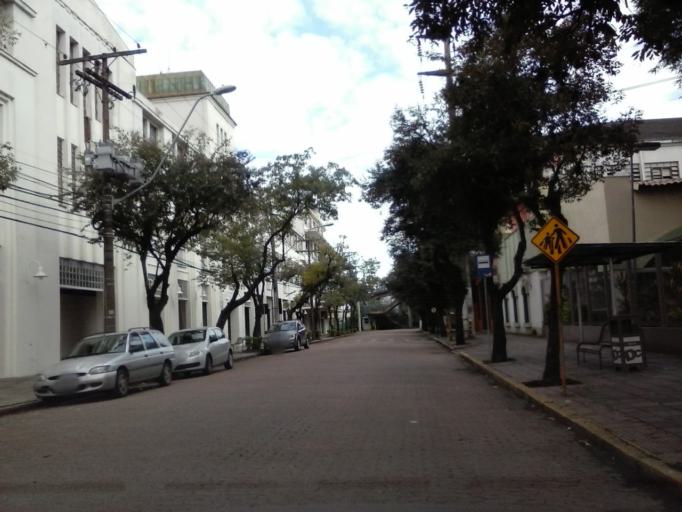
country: BR
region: Rio Grande do Sul
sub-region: Porto Alegre
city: Porto Alegre
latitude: -29.9964
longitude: -51.2024
